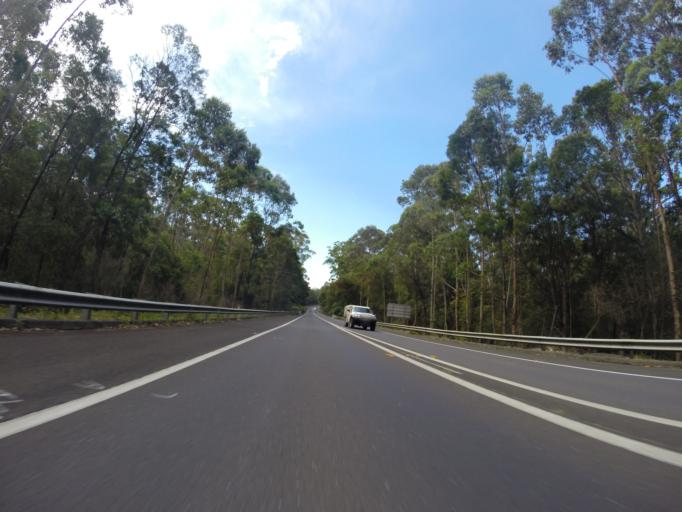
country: AU
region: New South Wales
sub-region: Shoalhaven Shire
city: Falls Creek
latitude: -35.0509
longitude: 150.5764
